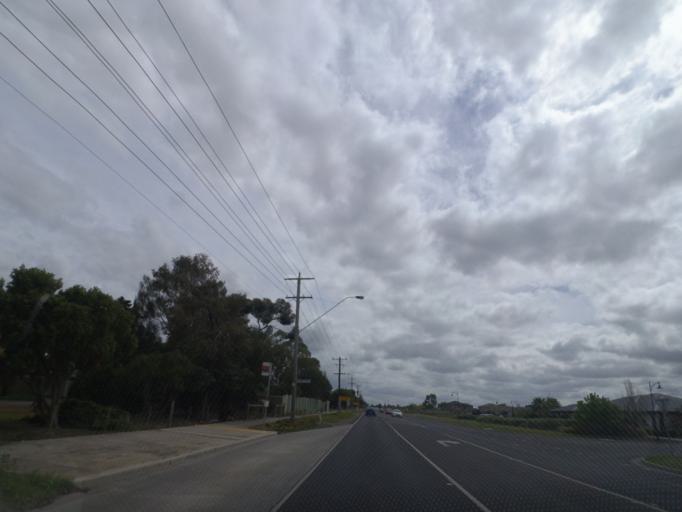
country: AU
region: Victoria
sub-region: Wyndham
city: Hoppers Crossing
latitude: -37.8495
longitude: 144.6966
